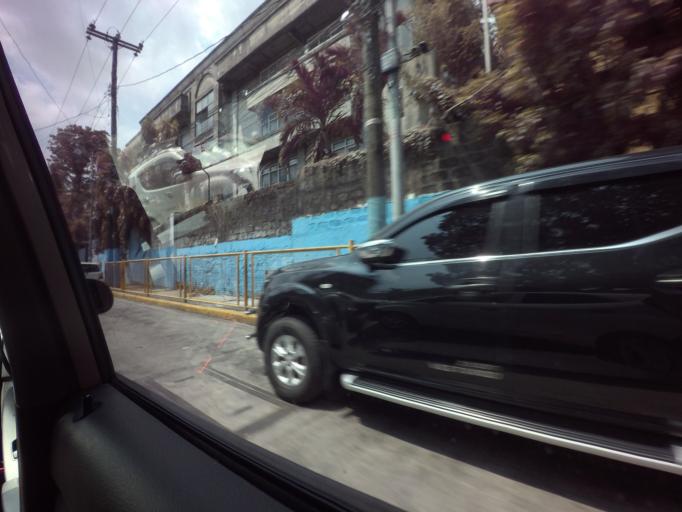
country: PH
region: Metro Manila
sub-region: San Juan
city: San Juan
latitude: 14.5901
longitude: 121.0127
